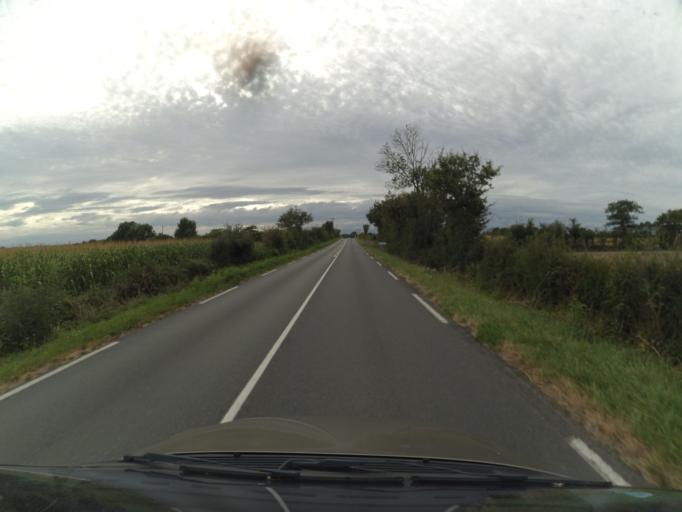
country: FR
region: Pays de la Loire
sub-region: Departement de la Vendee
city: Mortagne-sur-Sevre
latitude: 47.0137
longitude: -0.9929
